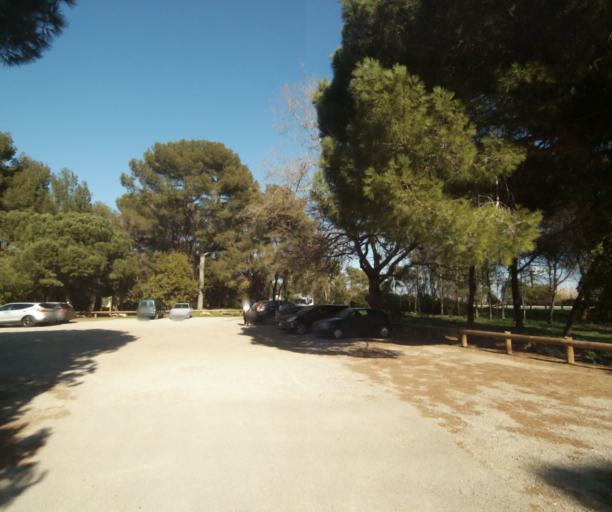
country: FR
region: Provence-Alpes-Cote d'Azur
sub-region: Departement des Alpes-Maritimes
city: Biot
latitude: 43.6185
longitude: 7.1283
